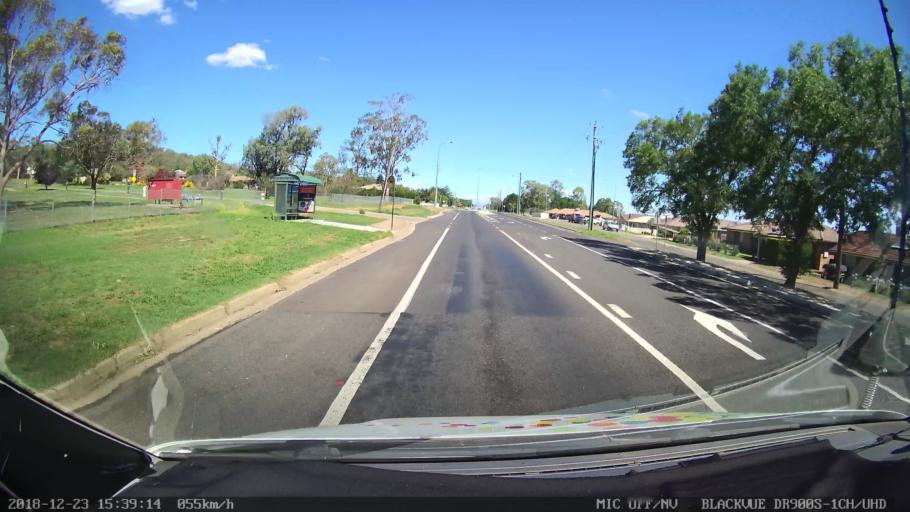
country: AU
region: New South Wales
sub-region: Tamworth Municipality
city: Tamworth
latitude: -31.0640
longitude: 150.9024
